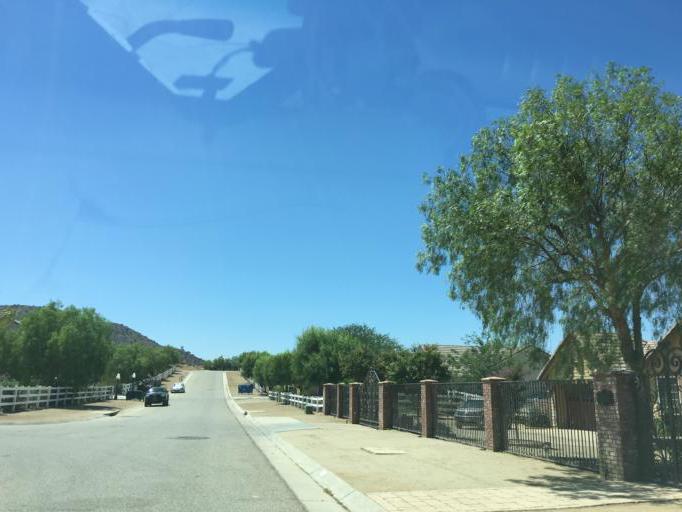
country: US
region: California
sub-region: Los Angeles County
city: Agua Dulce
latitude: 34.5133
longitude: -118.3073
